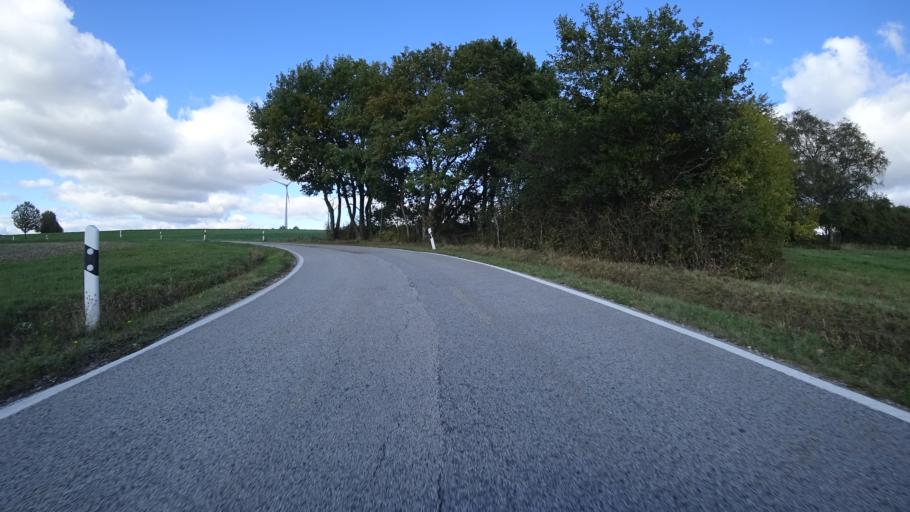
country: DE
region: Rheinland-Pfalz
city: Neuerkirch
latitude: 50.0189
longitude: 7.5019
